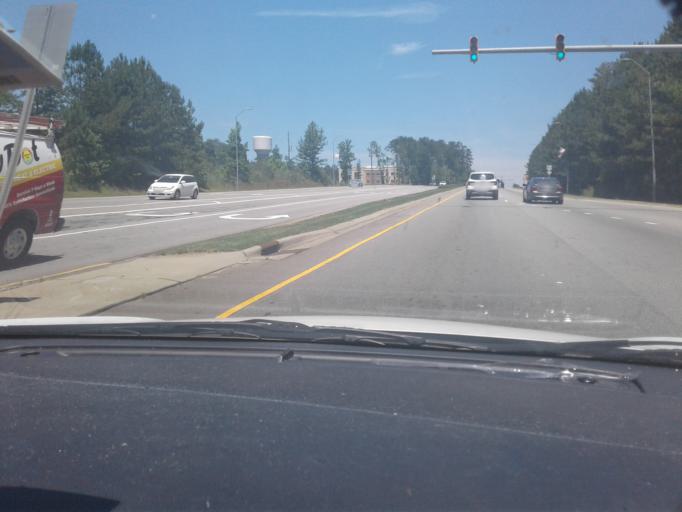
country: US
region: North Carolina
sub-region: Wake County
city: Holly Springs
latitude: 35.6539
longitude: -78.8479
